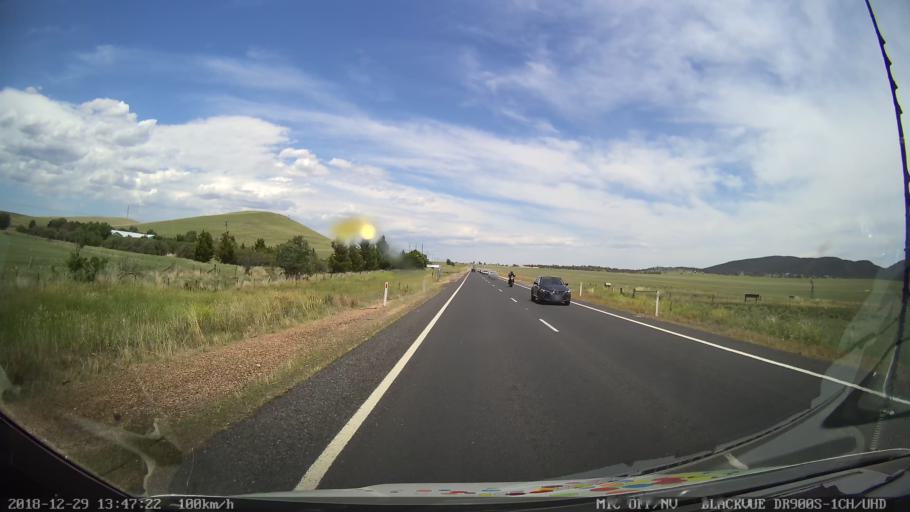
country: AU
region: New South Wales
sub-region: Cooma-Monaro
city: Cooma
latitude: -36.1256
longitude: 149.1425
